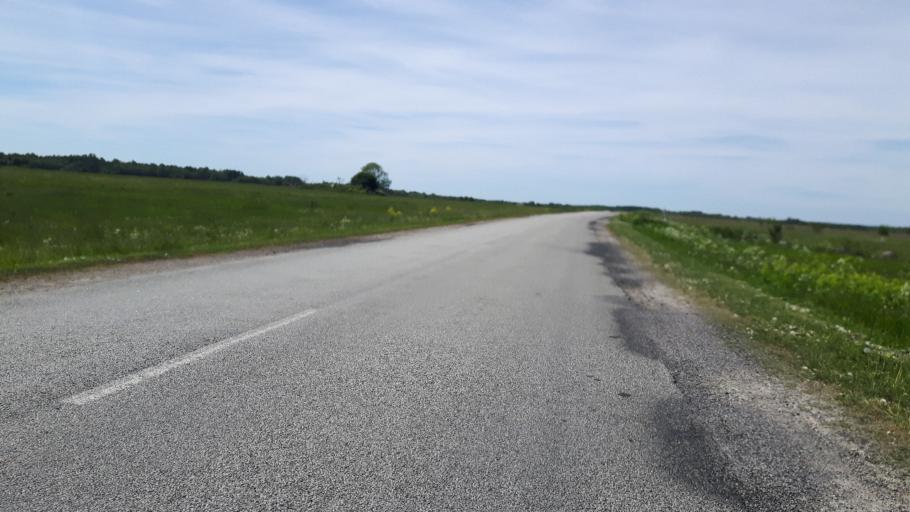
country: EE
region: Harju
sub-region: Kuusalu vald
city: Kuusalu
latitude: 59.4599
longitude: 25.3418
